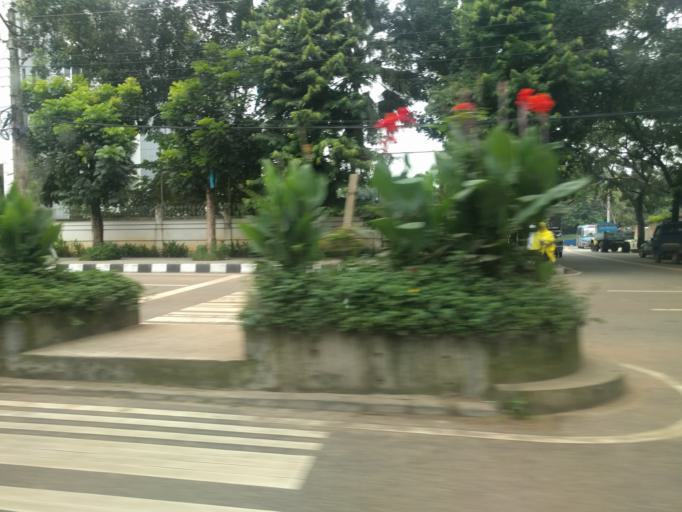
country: BD
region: Dhaka
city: Paltan
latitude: 23.7976
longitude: 90.4131
